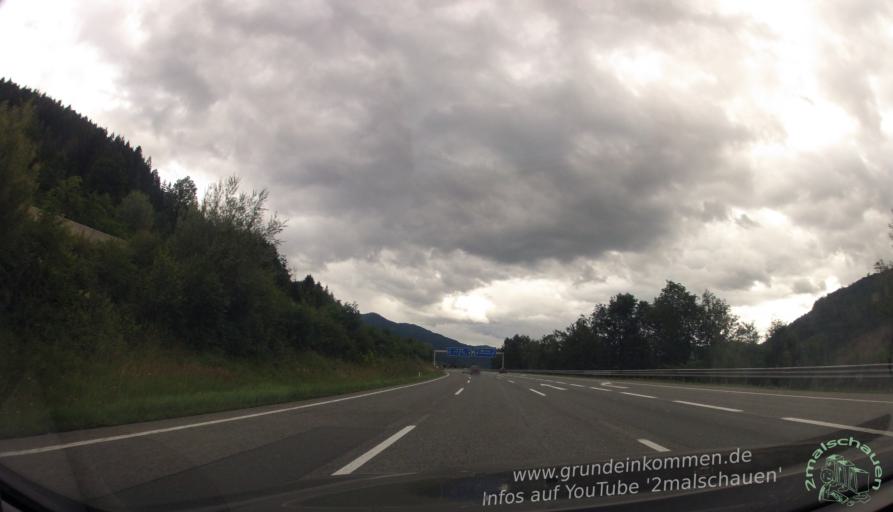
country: AT
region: Salzburg
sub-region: Politischer Bezirk Sankt Johann im Pongau
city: Pfarrwerfen
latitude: 47.4449
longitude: 13.2184
